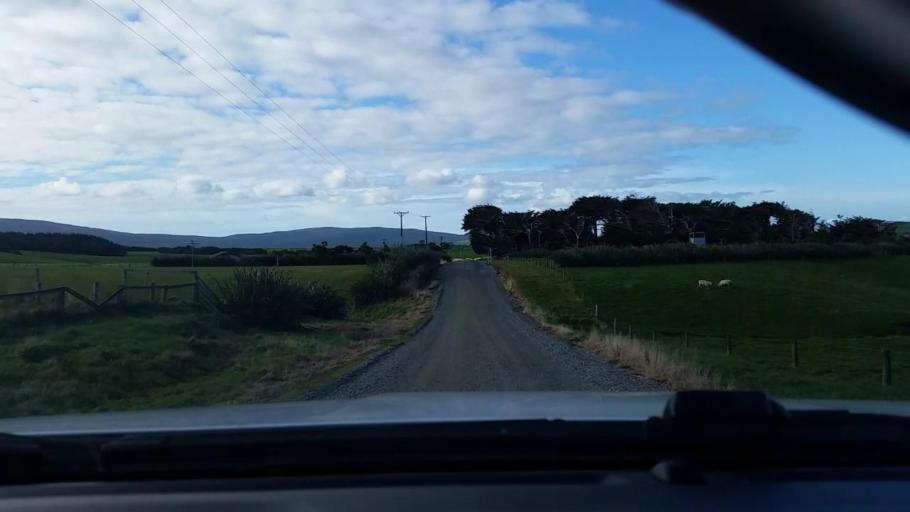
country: NZ
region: Southland
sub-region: Southland District
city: Riverton
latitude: -46.3303
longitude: 167.7128
